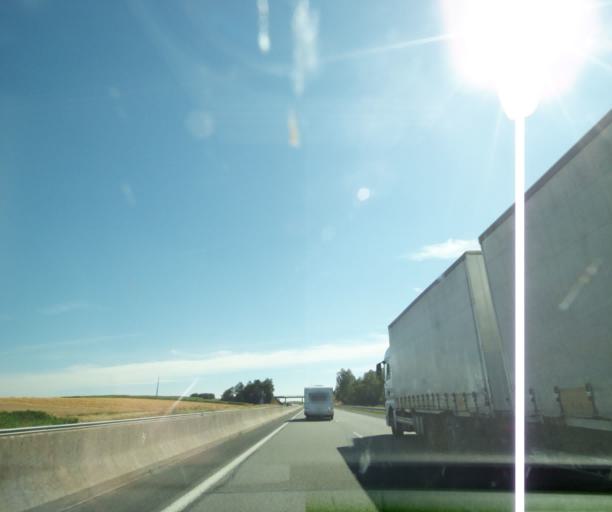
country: FR
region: Lorraine
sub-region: Departement des Vosges
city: Bulgneville
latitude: 48.1788
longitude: 5.7386
